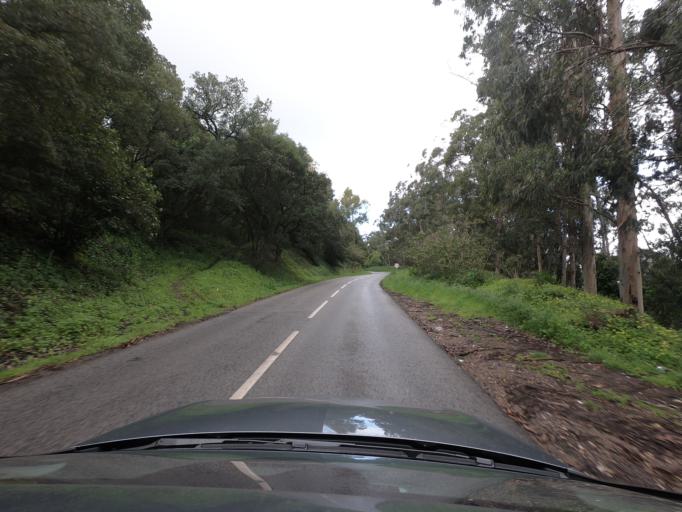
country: PT
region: Lisbon
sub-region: Sintra
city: Queluz
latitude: 38.7461
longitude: -9.2609
